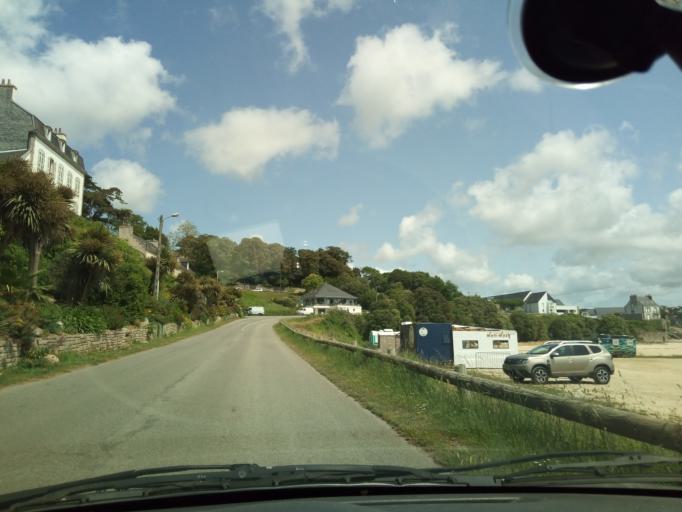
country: FR
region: Brittany
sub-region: Departement du Finistere
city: Audierne
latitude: 48.0164
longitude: -4.5384
